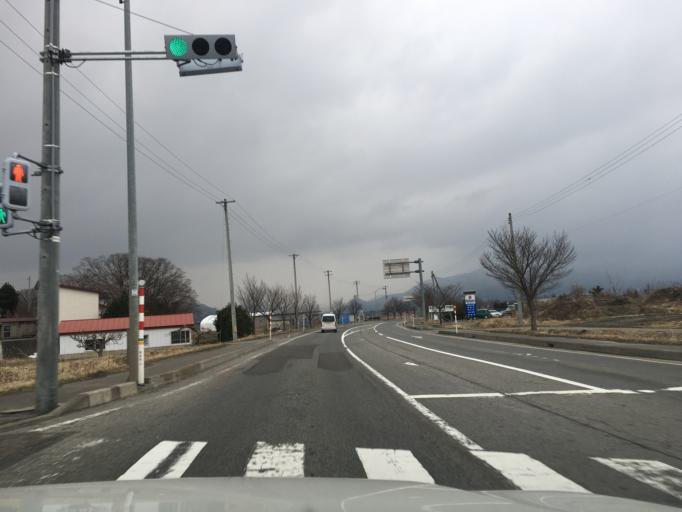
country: JP
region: Aomori
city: Kuroishi
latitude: 40.5722
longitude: 140.5680
